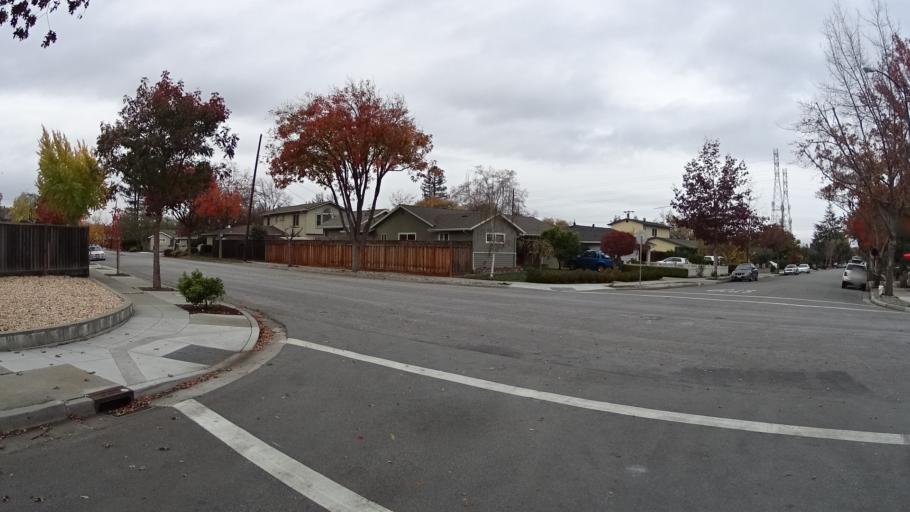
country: US
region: California
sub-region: Santa Clara County
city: Sunnyvale
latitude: 37.3678
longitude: -122.0529
